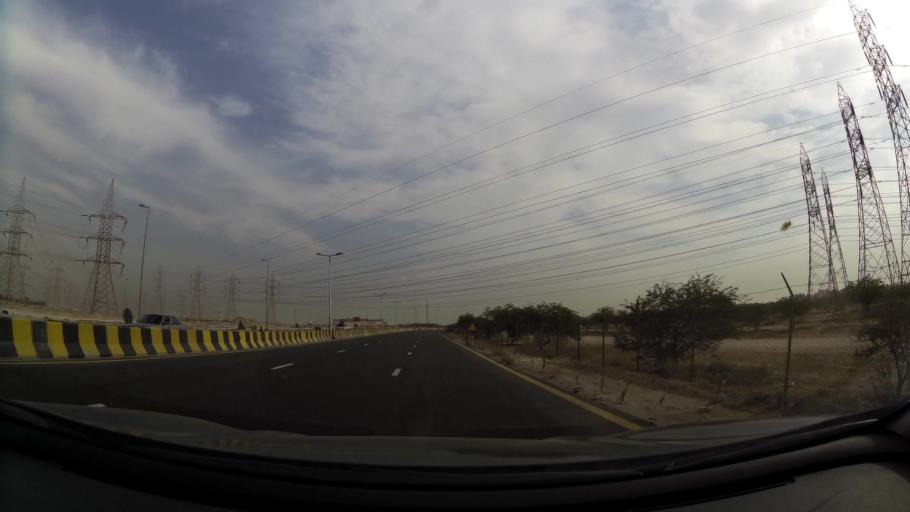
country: KW
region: Muhafazat al Jahra'
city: Al Jahra'
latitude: 29.3325
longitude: 47.7935
